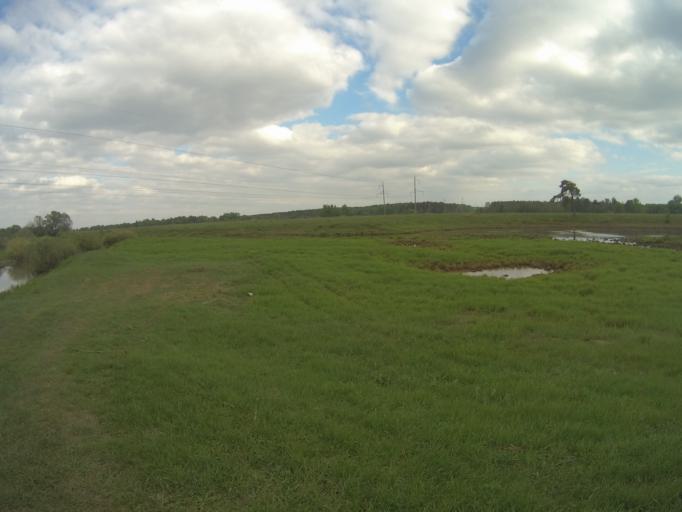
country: RU
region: Vladimir
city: Raduzhnyy
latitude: 56.0335
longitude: 40.2380
